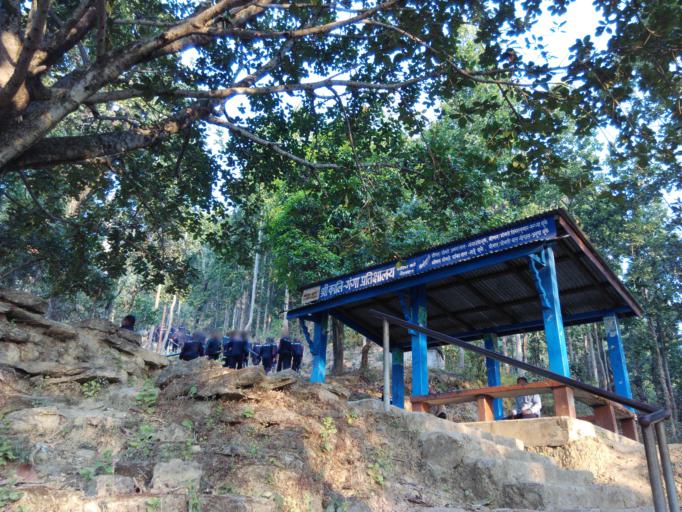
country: NP
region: Central Region
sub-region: Narayani Zone
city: Bharatpur
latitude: 27.7224
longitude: 84.4186
